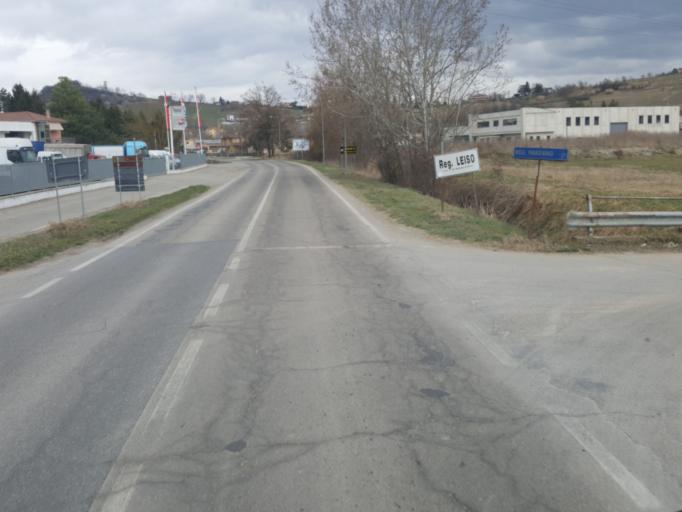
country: IT
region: Piedmont
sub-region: Provincia di Asti
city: San Marzano Oliveto
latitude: 44.7494
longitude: 8.2849
